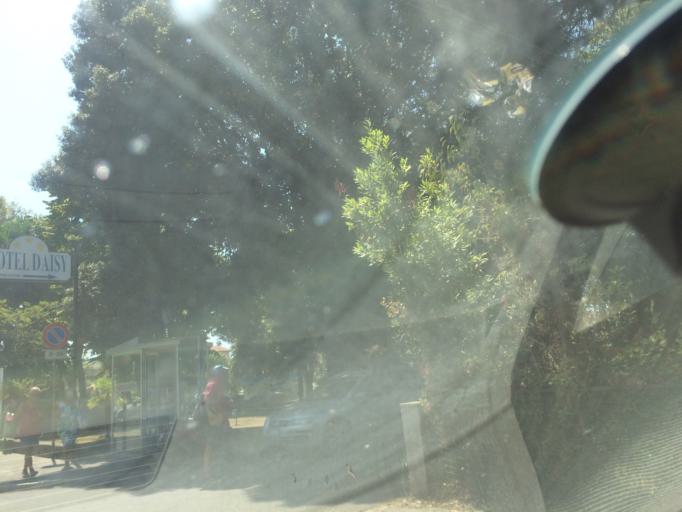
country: IT
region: Tuscany
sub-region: Provincia di Massa-Carrara
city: Massa
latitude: 44.0112
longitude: 10.0979
